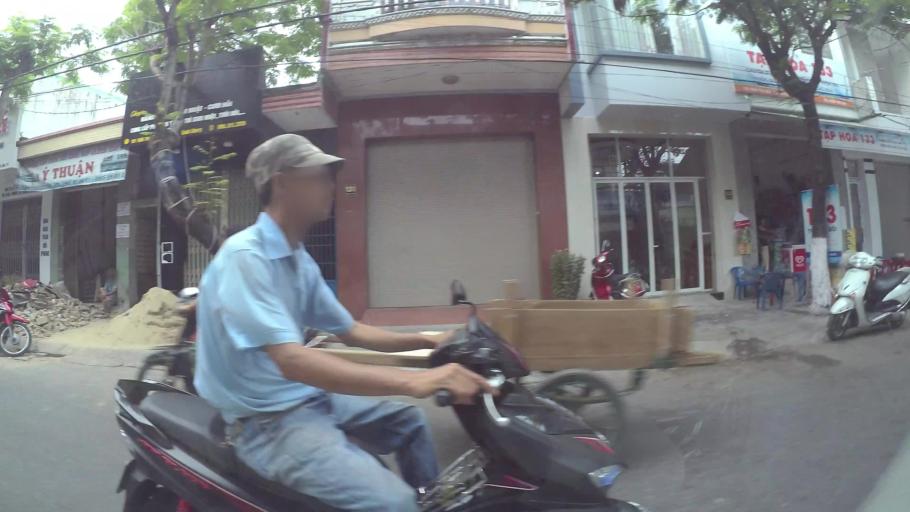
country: VN
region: Da Nang
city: Thanh Khe
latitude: 16.0683
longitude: 108.1976
